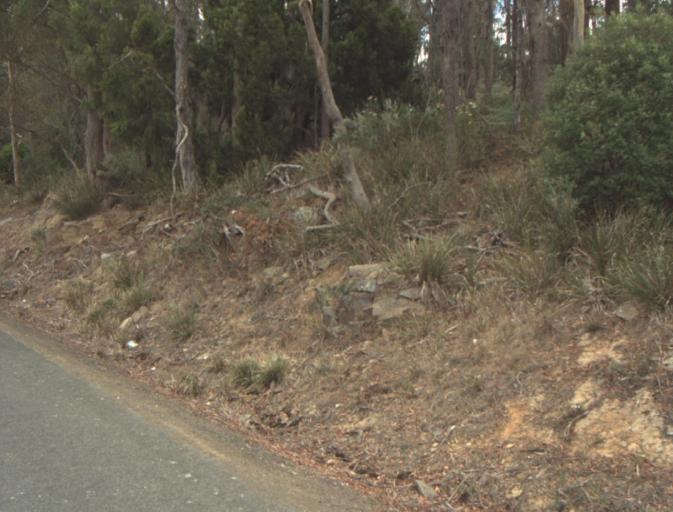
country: AU
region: Tasmania
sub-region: Launceston
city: Mayfield
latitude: -41.2383
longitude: 147.1969
